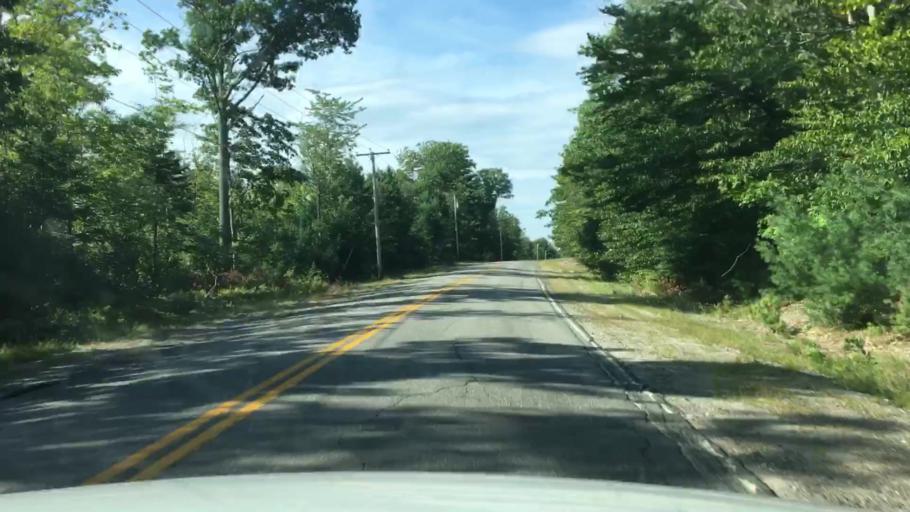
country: US
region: Maine
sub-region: Penobscot County
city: Enfield
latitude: 45.2271
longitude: -68.5417
